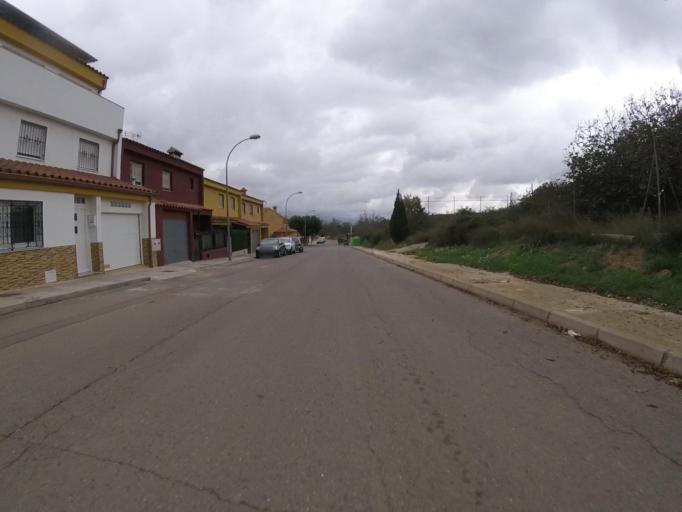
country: ES
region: Valencia
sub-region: Provincia de Castello
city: Cabanes
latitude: 40.1575
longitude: 0.0466
